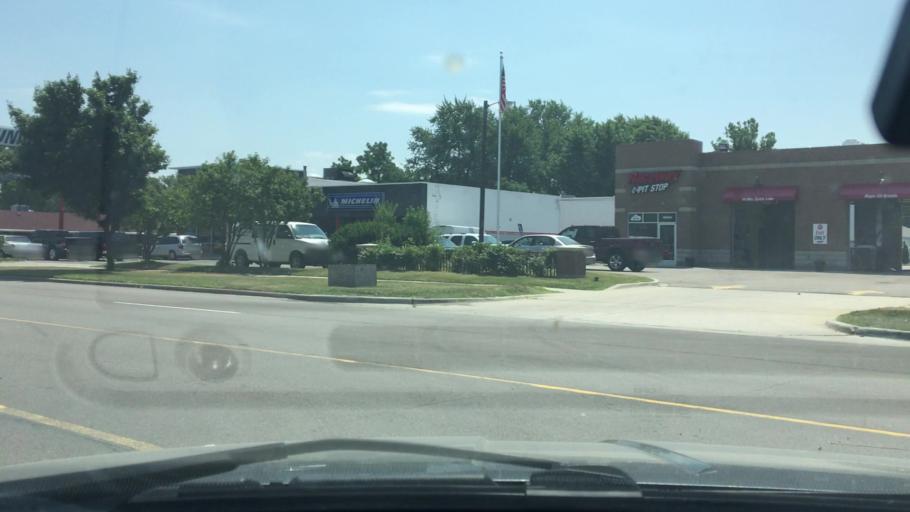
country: US
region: Michigan
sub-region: Wayne County
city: Redford
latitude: 42.3696
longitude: -83.3205
